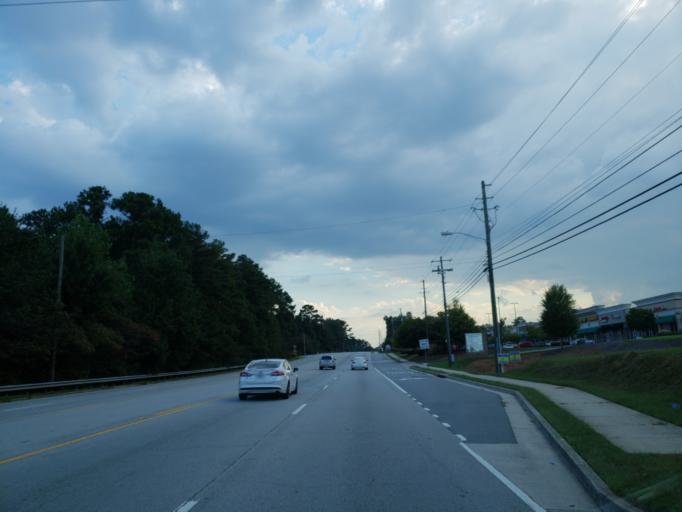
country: US
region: Georgia
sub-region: Cobb County
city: Fair Oaks
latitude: 33.9020
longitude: -84.6057
